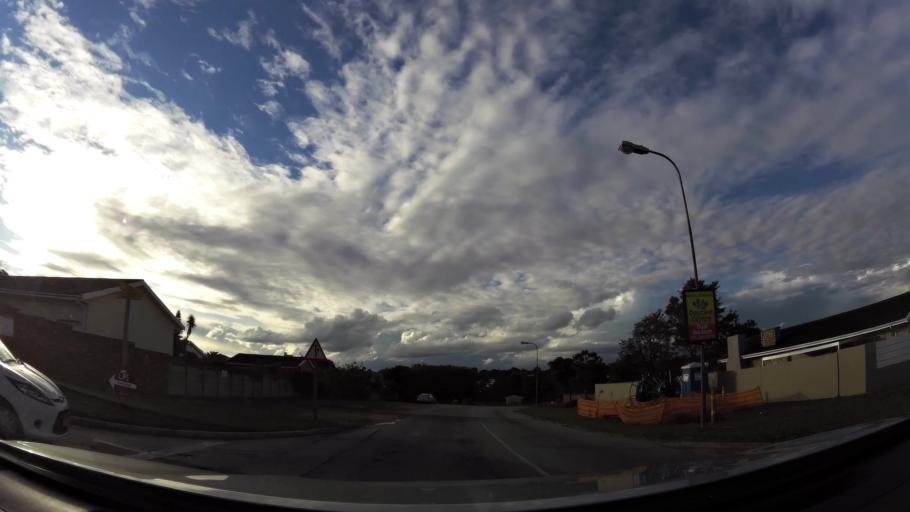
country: ZA
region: Eastern Cape
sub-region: Nelson Mandela Bay Metropolitan Municipality
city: Port Elizabeth
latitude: -33.9556
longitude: 25.5045
